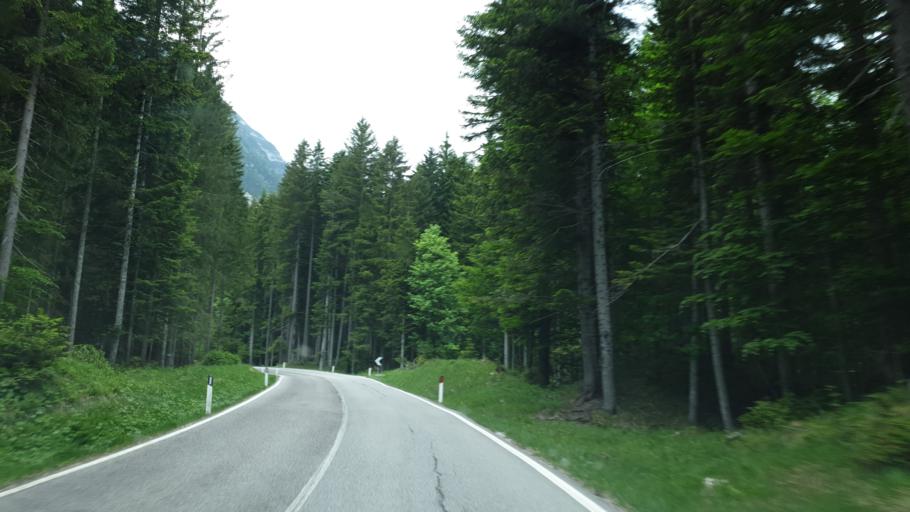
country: IT
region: Veneto
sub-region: Provincia di Belluno
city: San Vito
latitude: 46.5329
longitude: 12.2679
